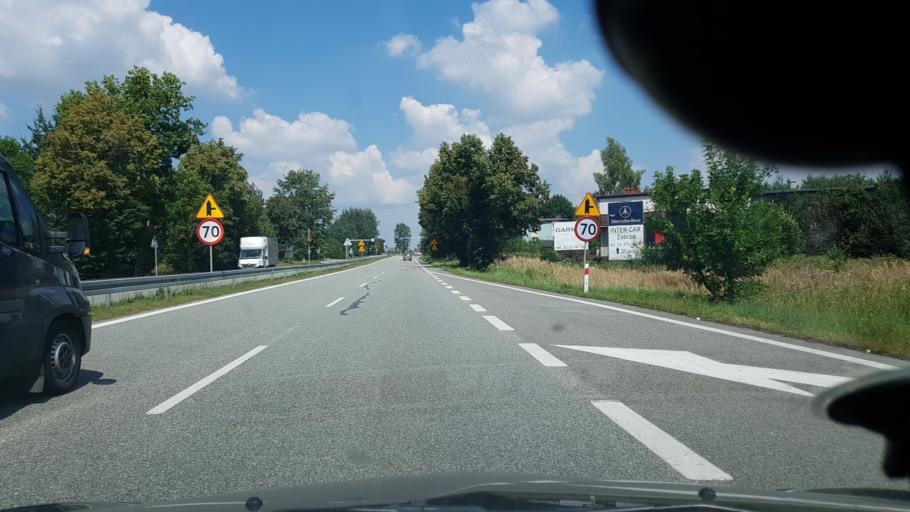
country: PL
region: Silesian Voivodeship
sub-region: Powiat pszczynski
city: Rudziczka
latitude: 50.0816
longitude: 18.7533
